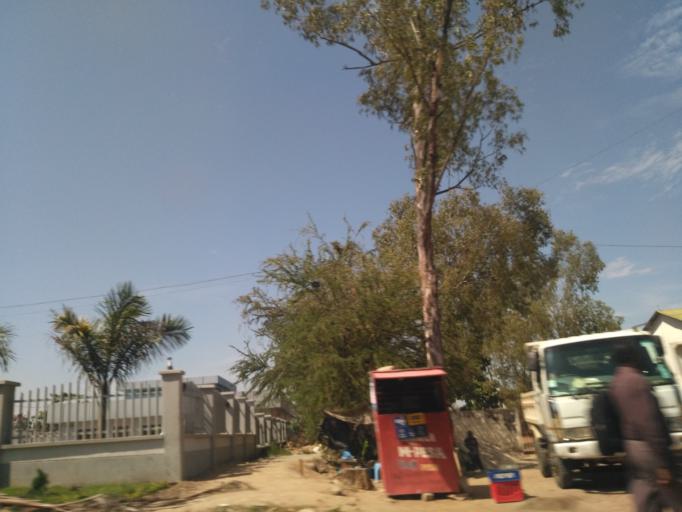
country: TZ
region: Mwanza
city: Mwanza
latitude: -2.4920
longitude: 32.9044
